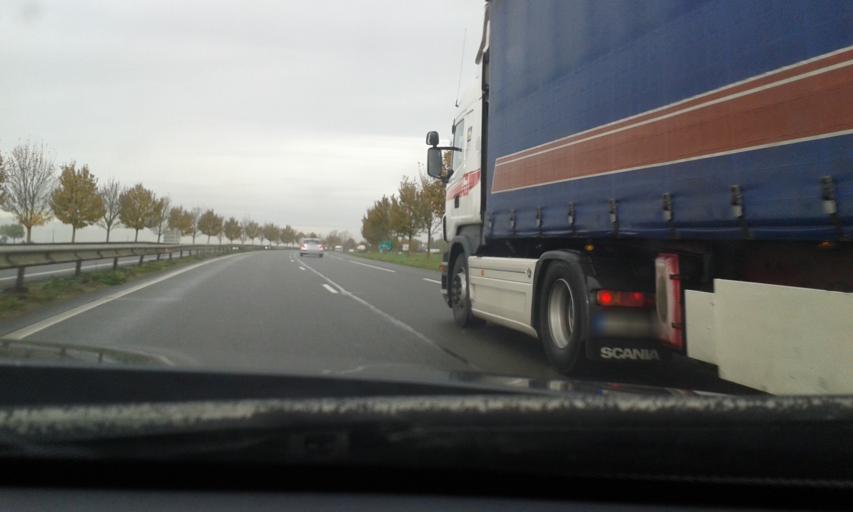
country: FR
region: Centre
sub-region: Departement d'Eure-et-Loir
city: Mainvilliers
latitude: 48.4306
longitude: 1.4317
